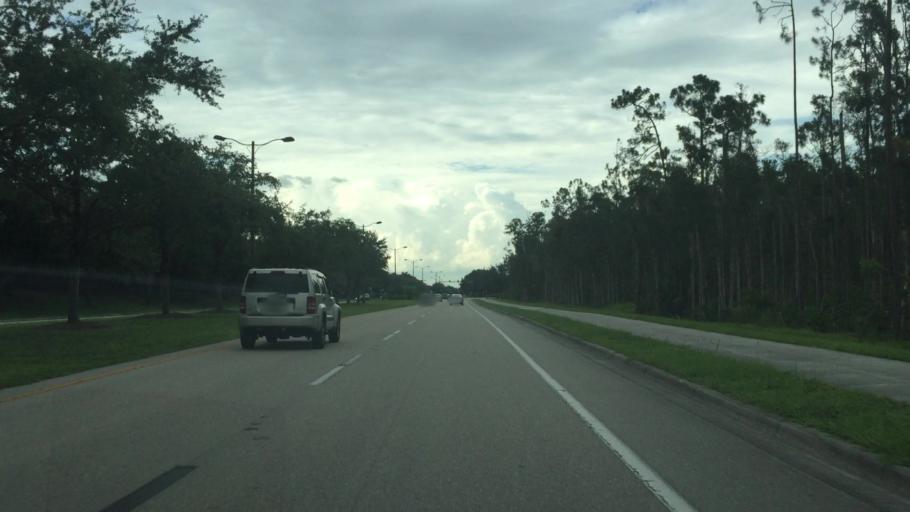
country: US
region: Florida
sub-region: Lee County
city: Three Oaks
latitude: 26.4672
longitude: -81.7859
